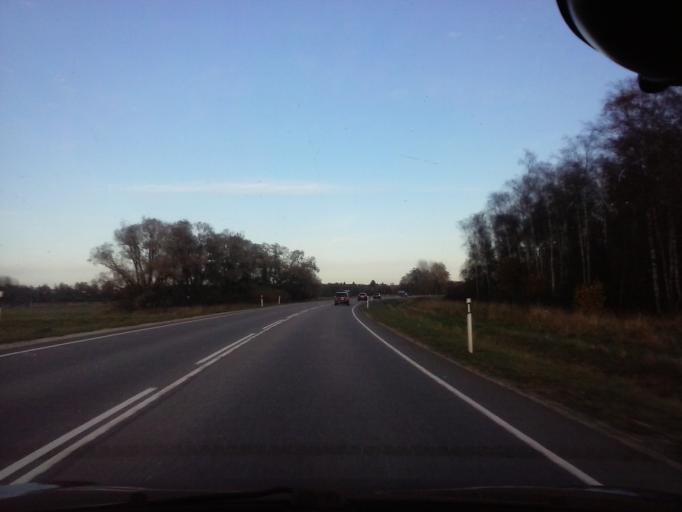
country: EE
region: Laeaene
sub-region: Ridala Parish
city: Uuemoisa
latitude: 58.9723
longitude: 23.8453
